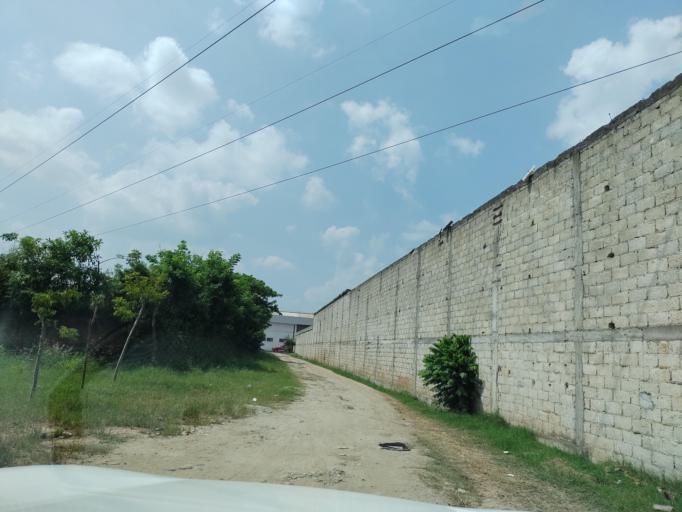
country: MX
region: Veracruz
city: Martinez de la Torre
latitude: 20.0786
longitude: -97.0455
